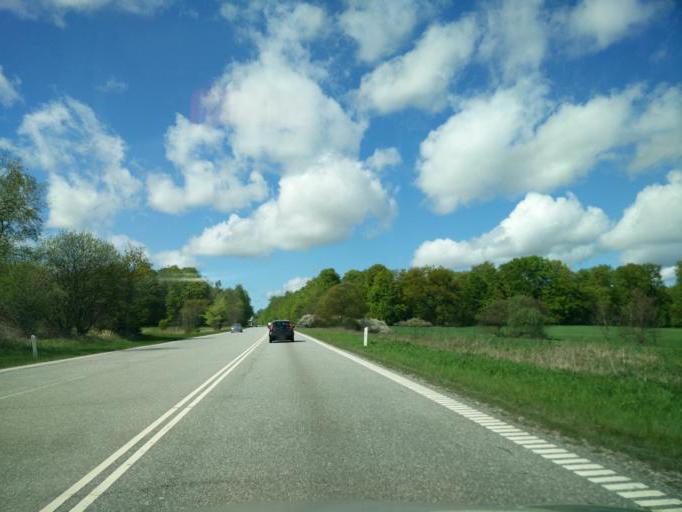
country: DK
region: Capital Region
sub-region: Hillerod Kommune
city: Hillerod
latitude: 55.8837
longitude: 12.3008
